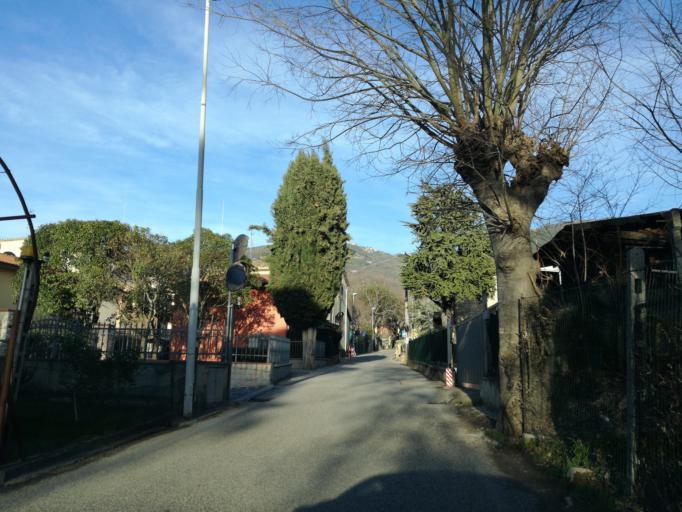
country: IT
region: Umbria
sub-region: Provincia di Perugia
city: Rivotorto
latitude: 43.0440
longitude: 12.6224
